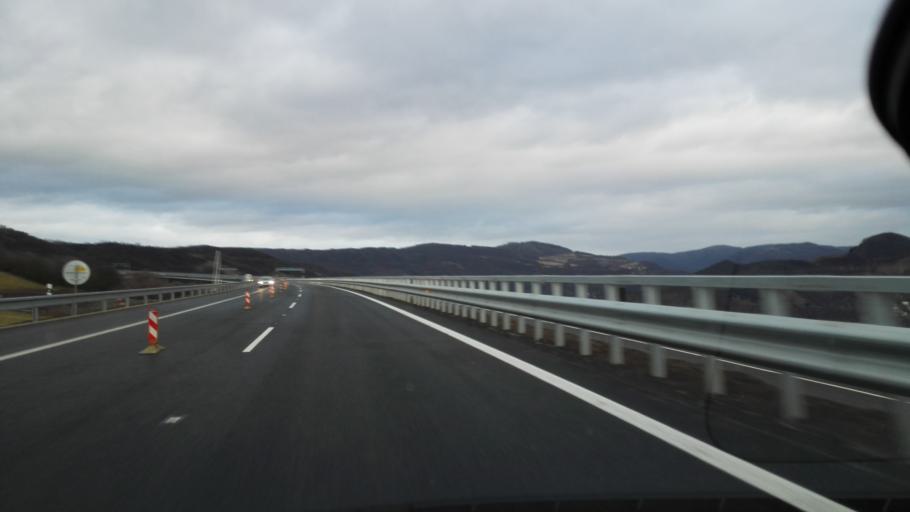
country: CZ
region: Ustecky
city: Velemin
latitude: 50.5687
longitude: 14.0196
